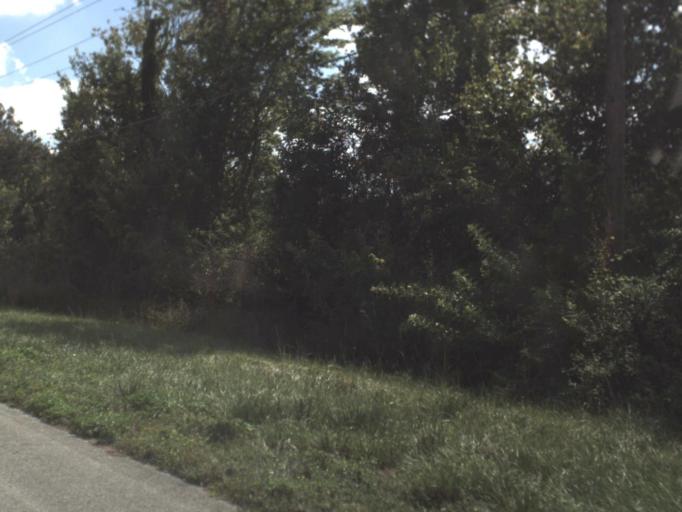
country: US
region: Florida
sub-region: Highlands County
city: Lake Placid
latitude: 27.4464
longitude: -81.2589
